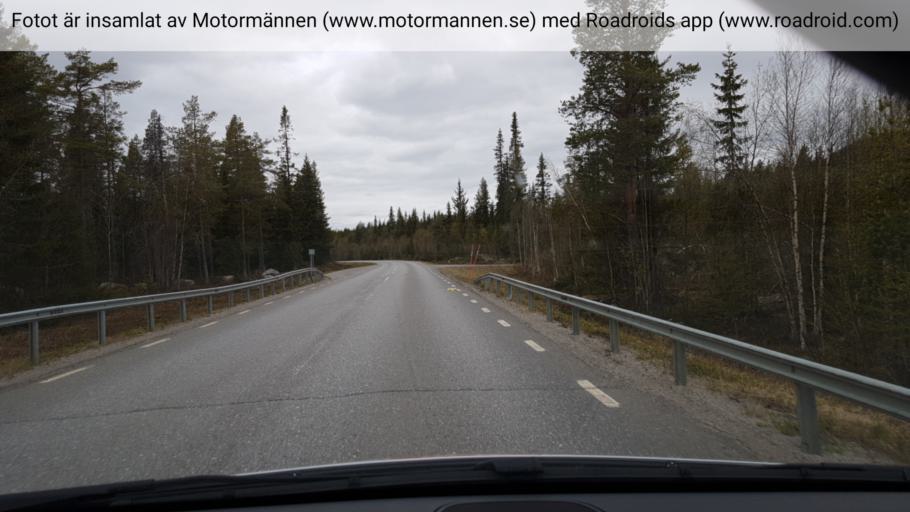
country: SE
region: Vaesterbotten
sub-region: Sorsele Kommun
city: Sorsele
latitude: 65.5055
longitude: 17.2495
